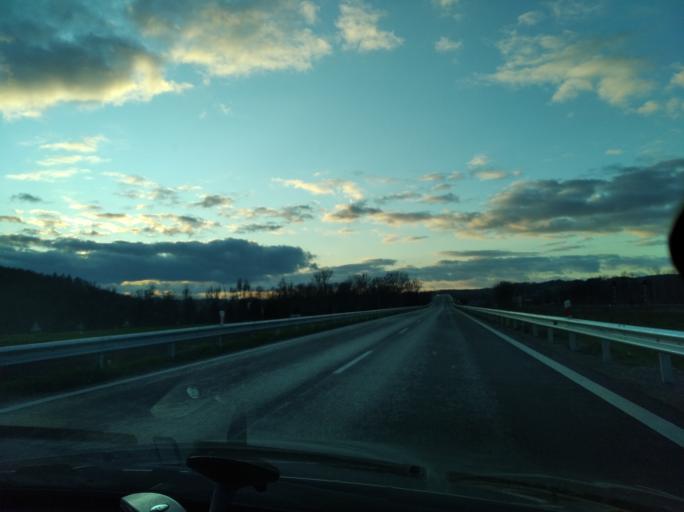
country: PL
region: Subcarpathian Voivodeship
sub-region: Powiat strzyzowski
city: Czudec
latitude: 49.9401
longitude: 21.8313
